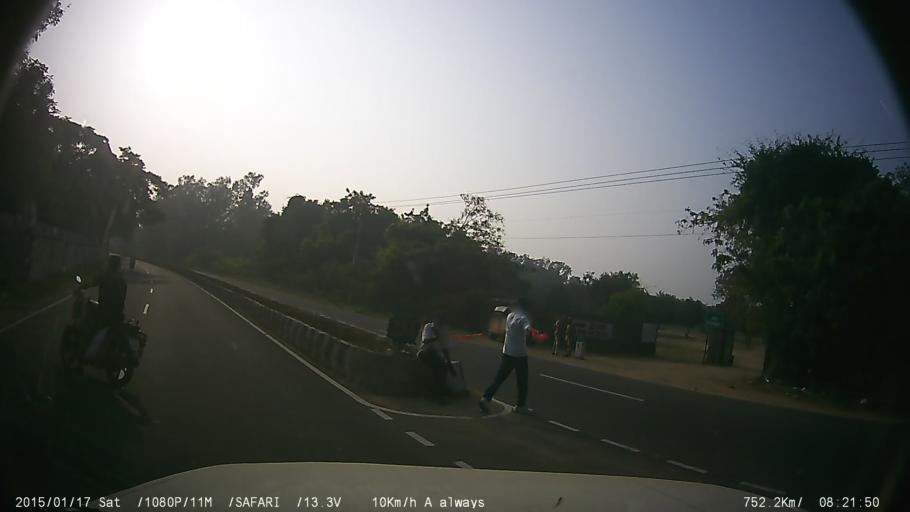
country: IN
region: Tamil Nadu
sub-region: Kancheepuram
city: Vandalur
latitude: 12.8754
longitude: 80.0883
